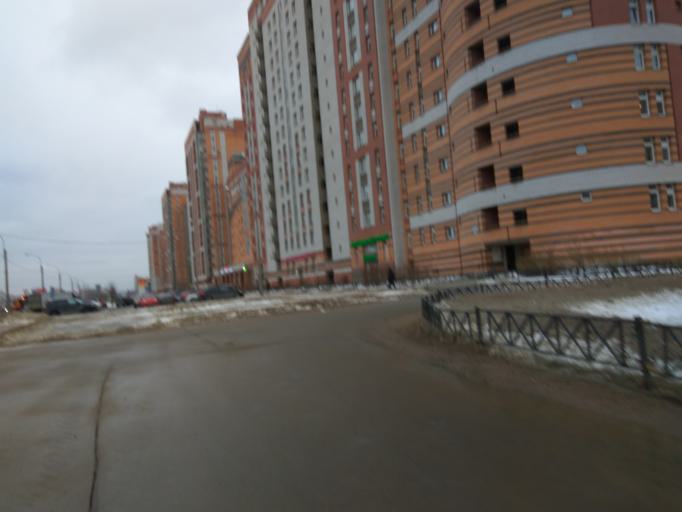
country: RU
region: St.-Petersburg
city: Staraya Derevnya
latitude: 60.0021
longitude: 30.2458
